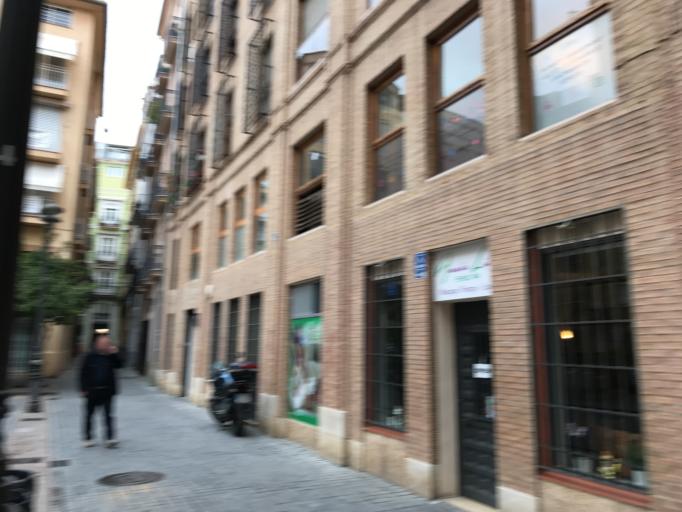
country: ES
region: Valencia
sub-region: Provincia de Valencia
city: Valencia
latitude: 39.4745
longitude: -0.3761
